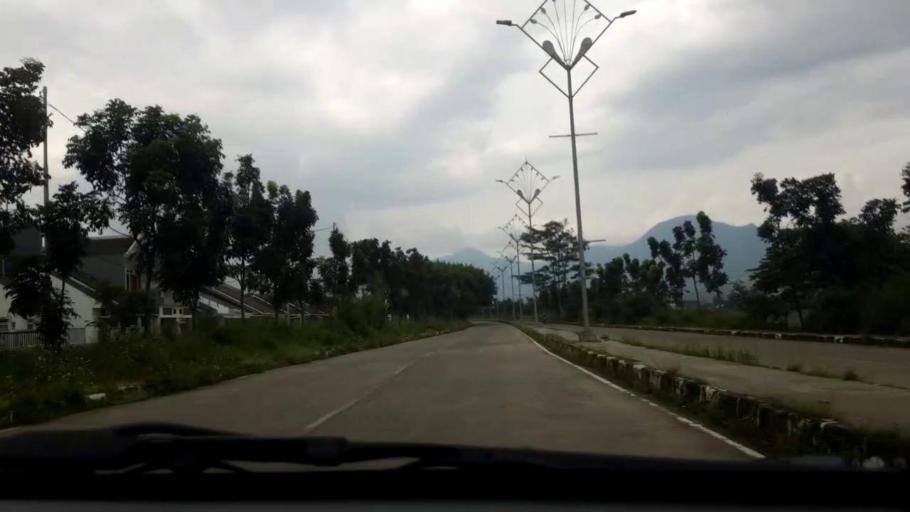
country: ID
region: West Java
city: Cileunyi
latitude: -6.9542
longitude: 107.7108
